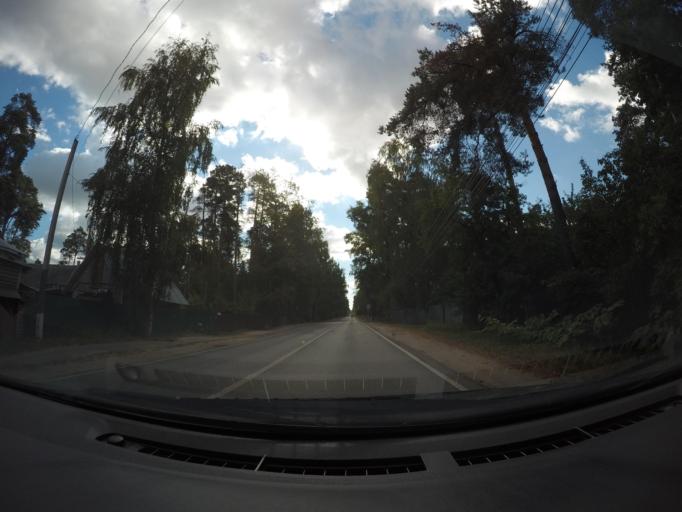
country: RU
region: Moskovskaya
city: Il'inskiy
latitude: 55.6282
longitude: 38.1074
